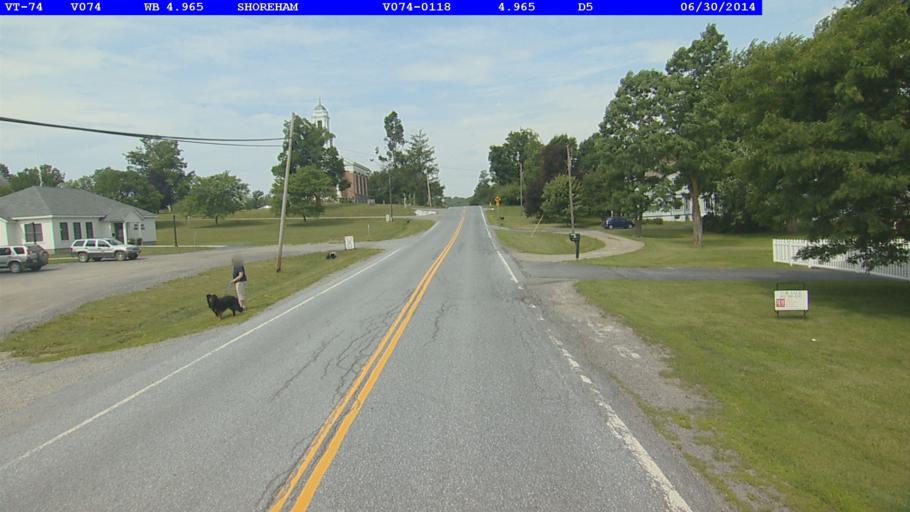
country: US
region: New York
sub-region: Essex County
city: Ticonderoga
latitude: 43.8938
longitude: -73.3146
